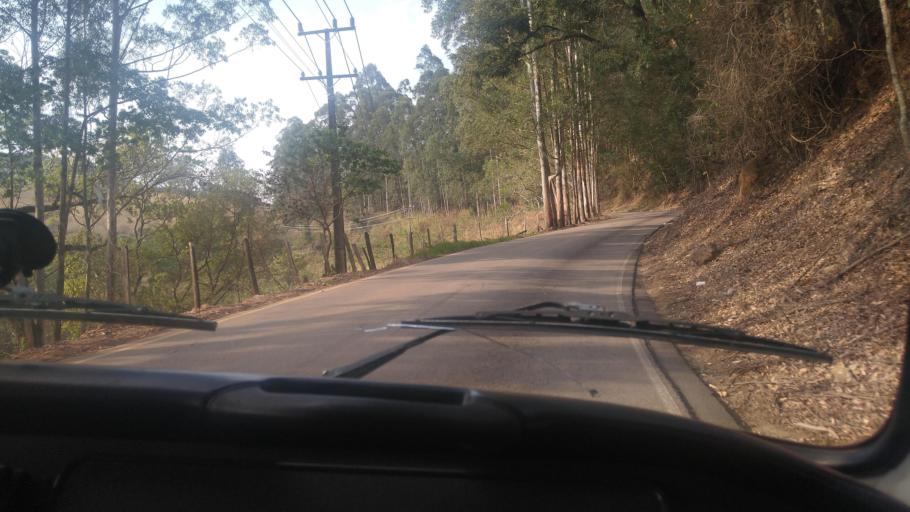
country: BR
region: Minas Gerais
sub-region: Extrema
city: Extrema
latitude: -22.7700
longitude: -46.4380
